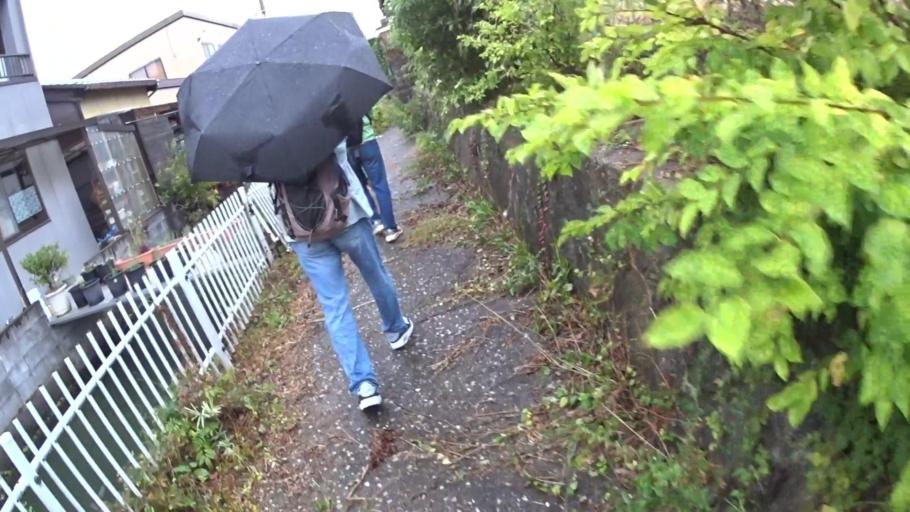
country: JP
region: Kyoto
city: Muko
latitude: 35.0136
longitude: 135.6895
